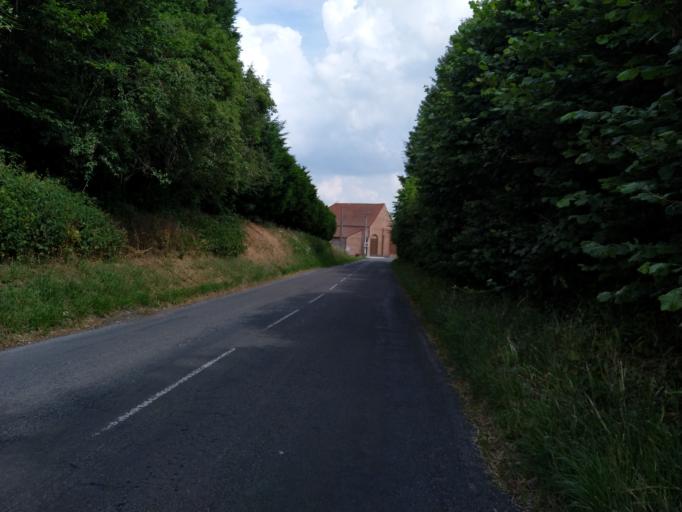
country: FR
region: Nord-Pas-de-Calais
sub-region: Departement du Nord
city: Rousies
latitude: 50.3190
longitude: 4.0040
